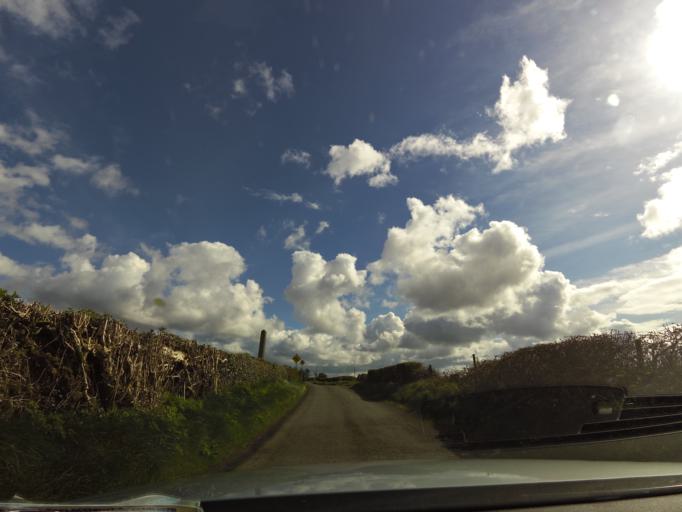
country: IE
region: Leinster
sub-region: Laois
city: Rathdowney
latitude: 52.7806
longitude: -7.5456
